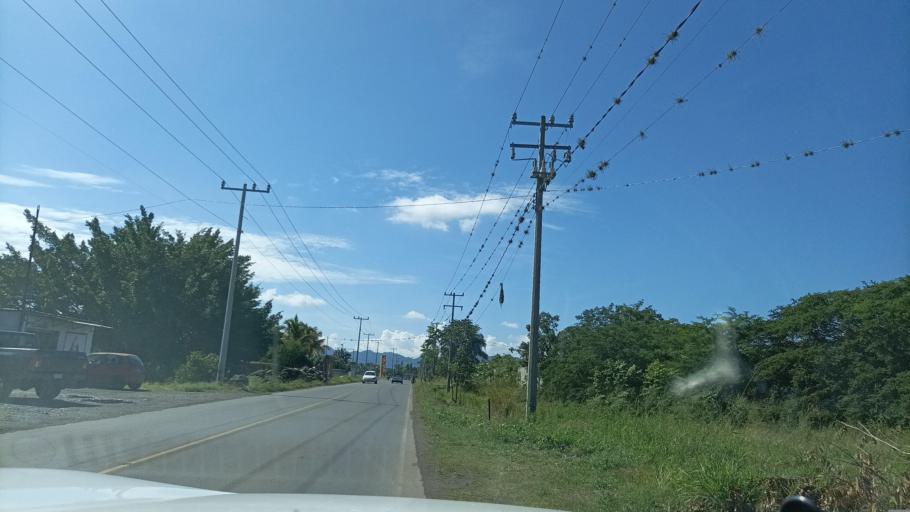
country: MX
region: Veracruz
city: Paso del Macho
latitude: 18.9671
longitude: -96.7333
